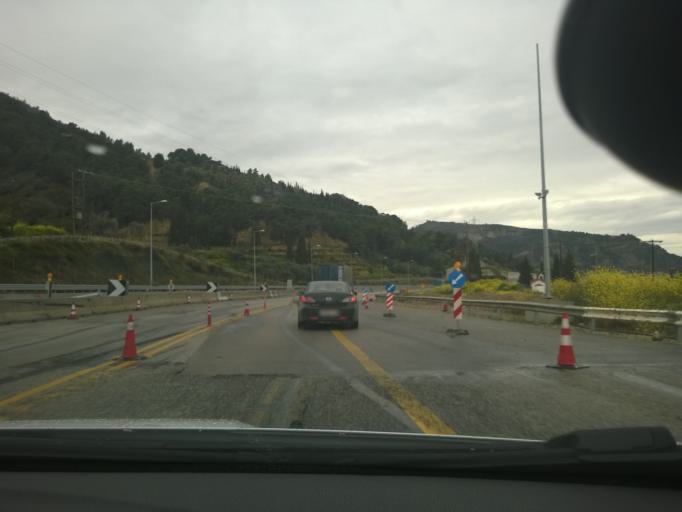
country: GR
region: West Greece
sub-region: Nomos Achaias
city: Aiyira
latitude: 38.1294
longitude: 22.4156
